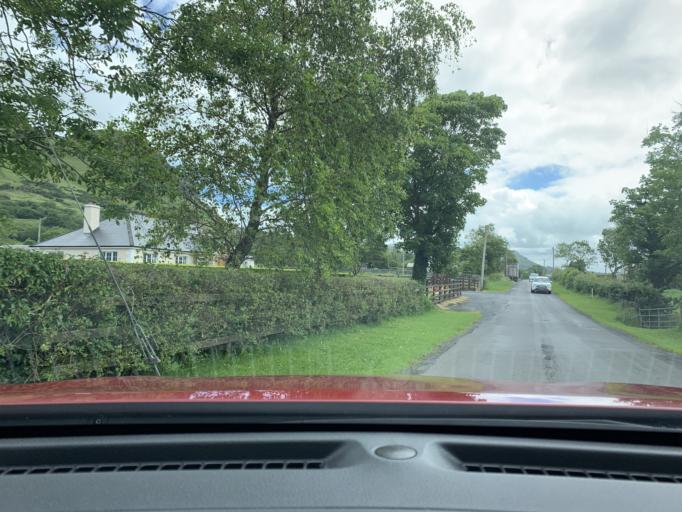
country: IE
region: Connaught
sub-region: Sligo
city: Sligo
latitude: 54.3398
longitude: -8.4798
